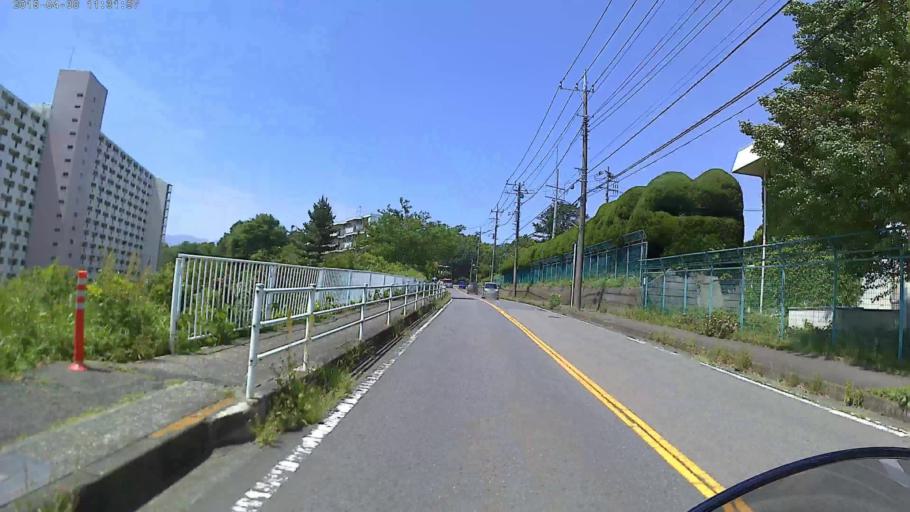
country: JP
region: Kanagawa
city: Zama
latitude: 35.4842
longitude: 139.4081
